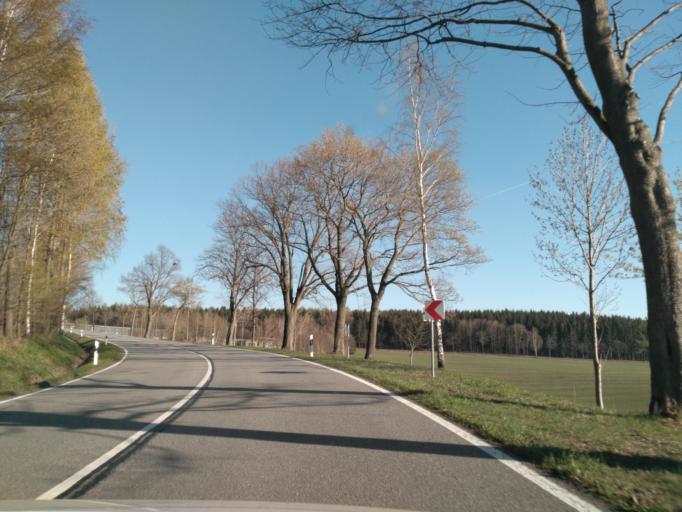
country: DE
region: Saxony
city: Schlettau
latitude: 50.5552
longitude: 12.9747
